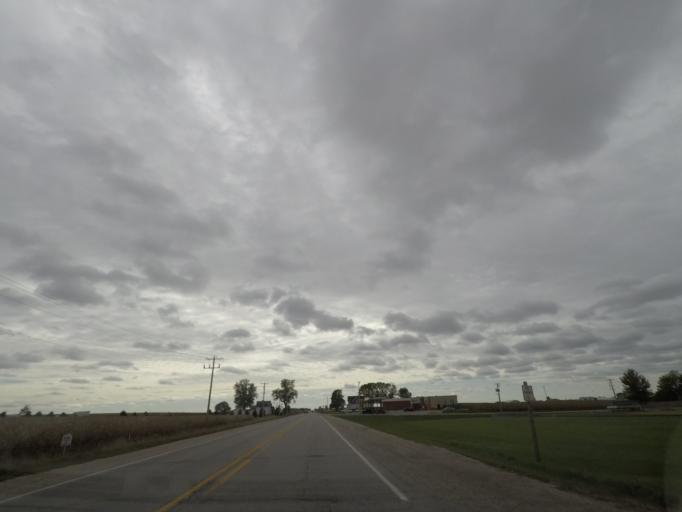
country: US
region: Iowa
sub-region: Story County
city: Nevada
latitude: 42.0164
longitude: -93.3095
